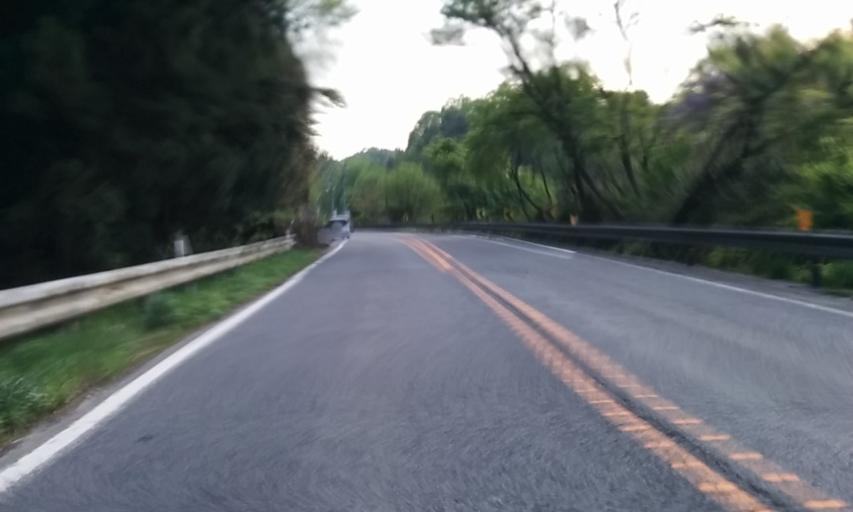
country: JP
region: Ehime
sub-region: Shikoku-chuo Shi
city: Matsuyama
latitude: 33.8003
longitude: 132.9672
